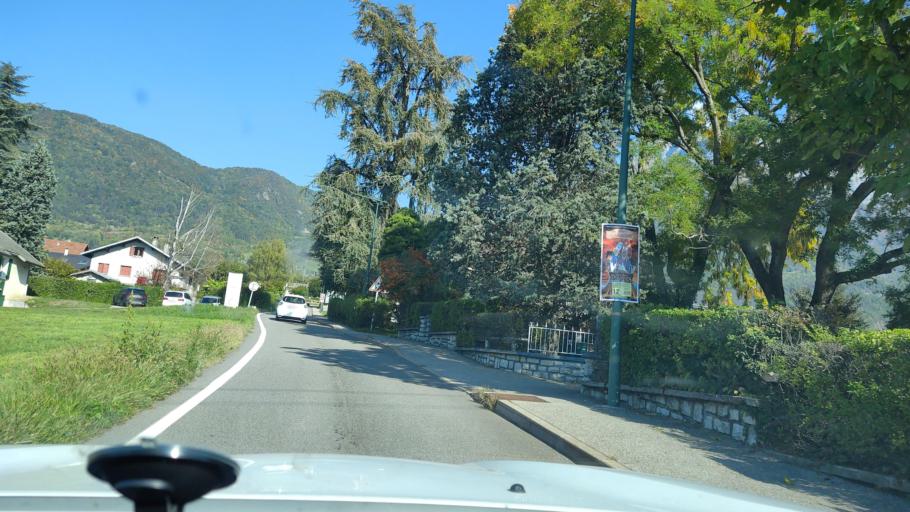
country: FR
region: Rhone-Alpes
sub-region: Departement de la Savoie
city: Coise-Saint-Jean-Pied-Gauthier
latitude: 45.5626
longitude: 6.1544
